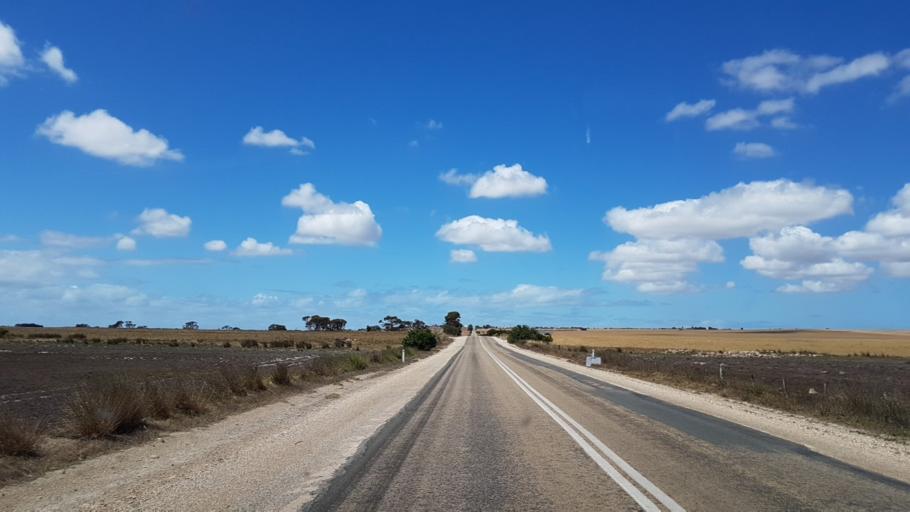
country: AU
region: South Australia
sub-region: Yorke Peninsula
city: Honiton
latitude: -34.9619
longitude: 137.4010
